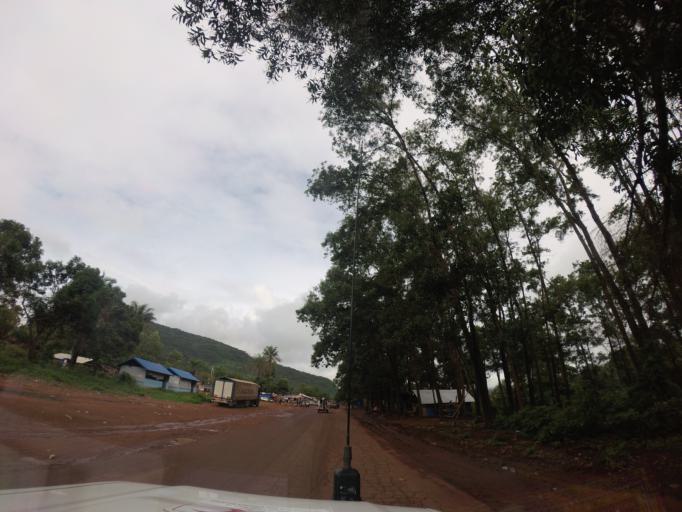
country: GN
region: Kindia
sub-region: Coyah
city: Coyah
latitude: 9.7848
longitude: -13.3167
